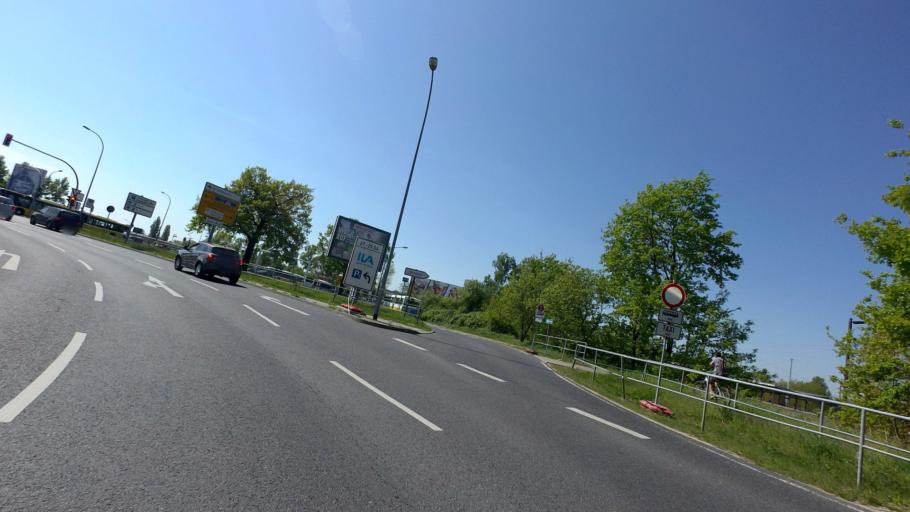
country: DE
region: Brandenburg
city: Schonefeld
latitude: 52.3919
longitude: 13.5160
